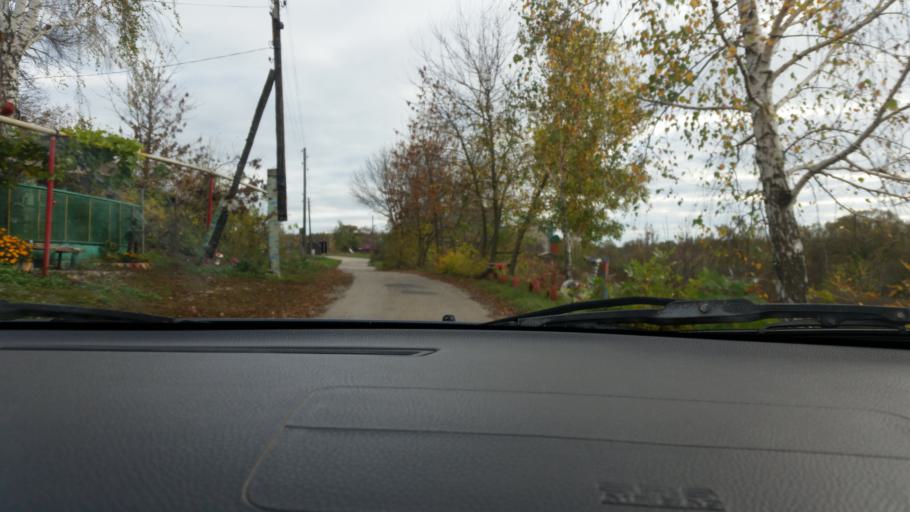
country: RU
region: Lipetsk
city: Gryazi
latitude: 52.4510
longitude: 39.9845
